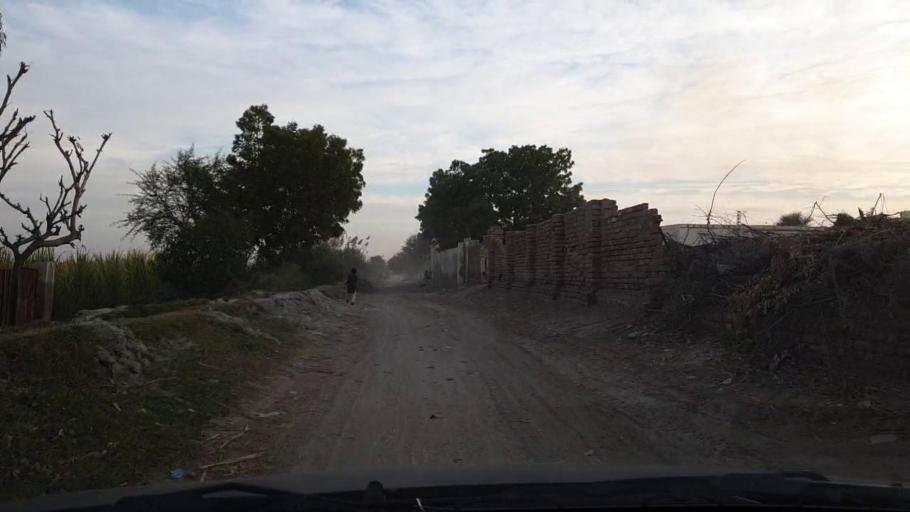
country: PK
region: Sindh
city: Khadro
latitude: 26.1288
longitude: 68.7778
